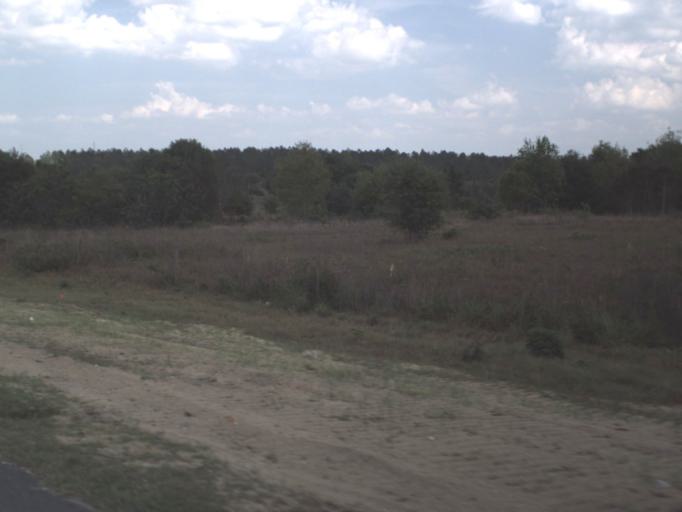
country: US
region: Florida
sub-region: Lake County
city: Howie In The Hills
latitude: 28.6394
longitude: -81.8104
